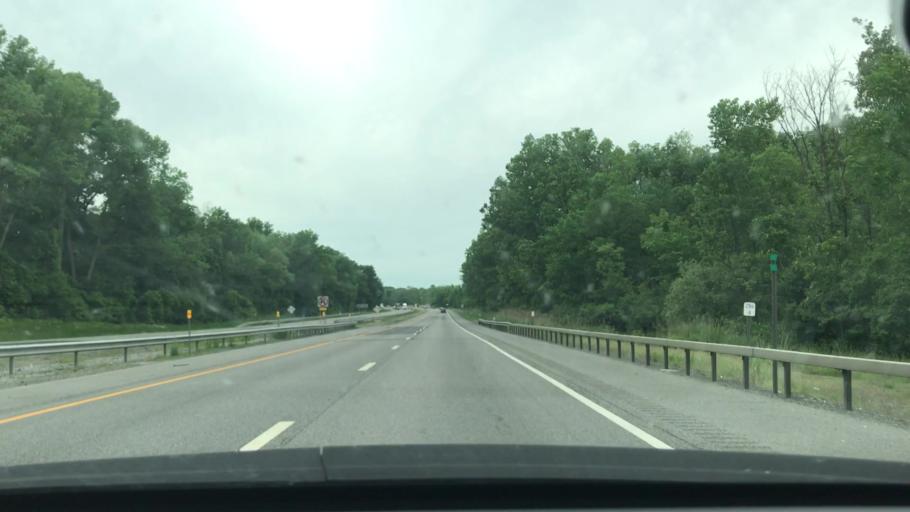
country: US
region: New York
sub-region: Onondaga County
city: Liverpool
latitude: 43.1181
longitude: -76.2266
